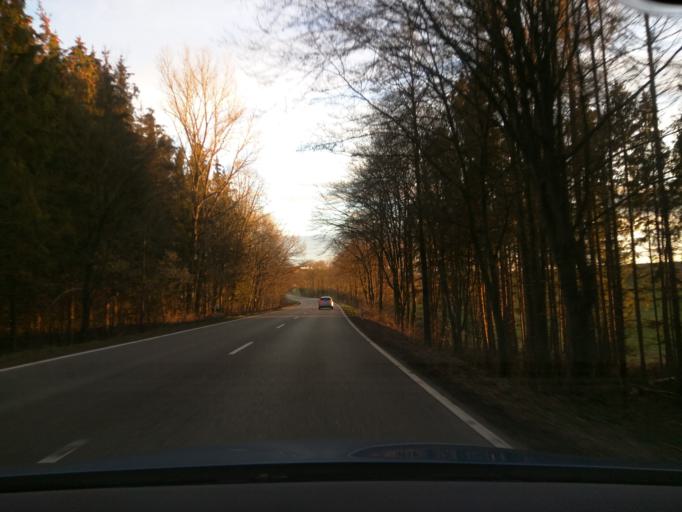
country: DE
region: Bavaria
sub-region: Upper Bavaria
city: Attenkirchen
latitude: 48.4975
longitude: 11.7618
